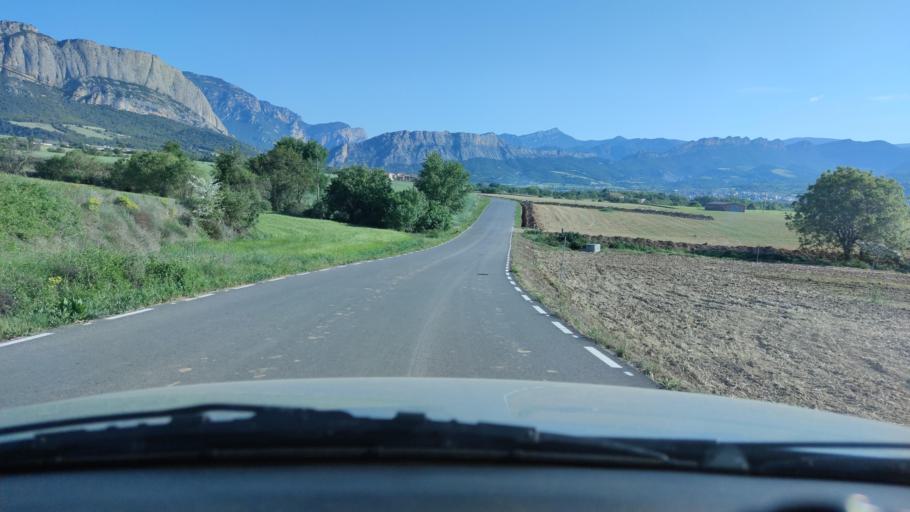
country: ES
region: Catalonia
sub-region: Provincia de Lleida
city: Oliana
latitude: 42.0521
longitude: 1.2943
